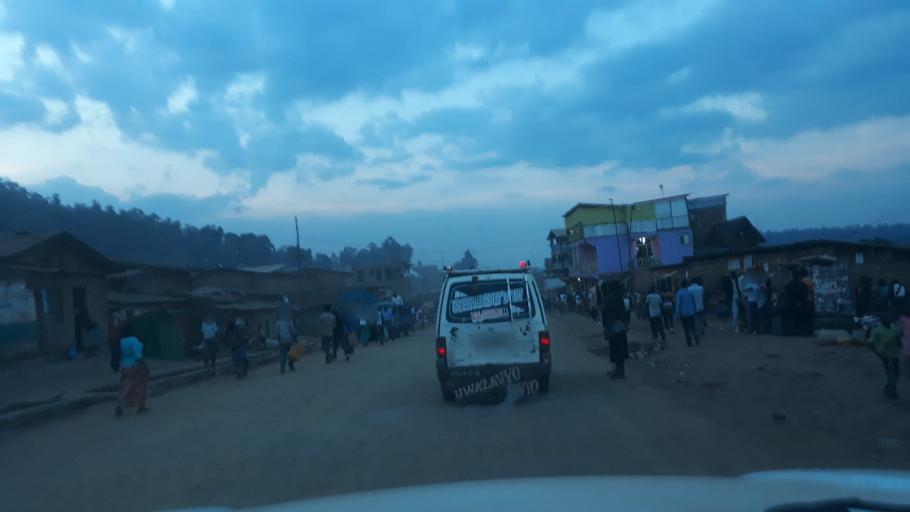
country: CD
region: South Kivu
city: Bukavu
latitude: -2.5458
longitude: 28.8641
